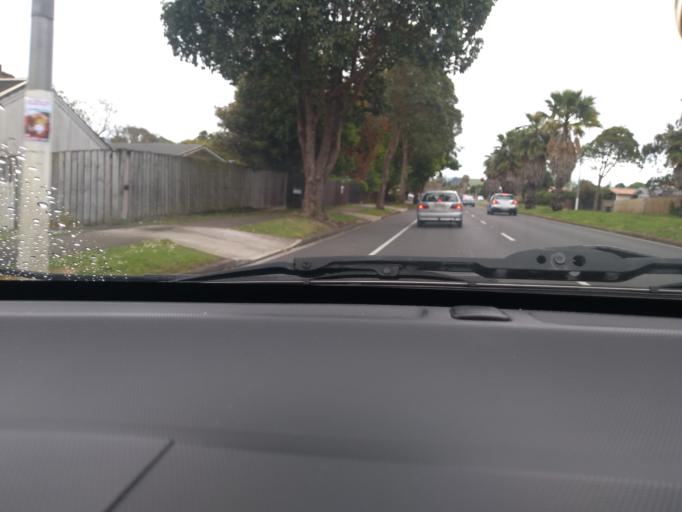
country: NZ
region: Auckland
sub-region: Auckland
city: Tamaki
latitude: -36.9215
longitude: 174.8785
